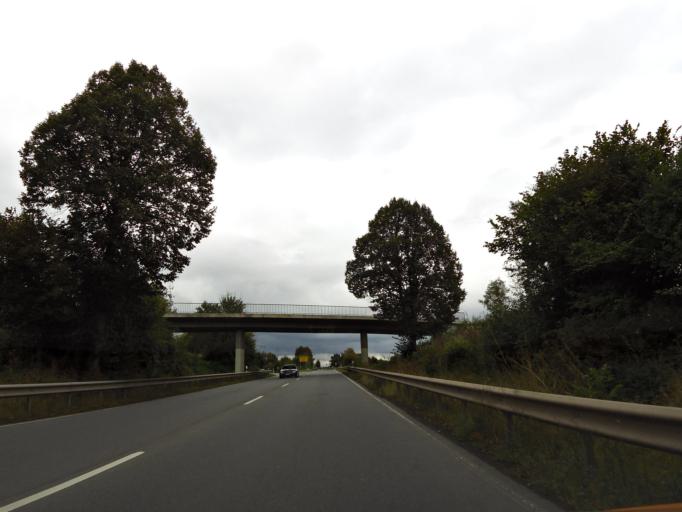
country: DE
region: Rheinland-Pfalz
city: Dreisen
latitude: 49.6055
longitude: 8.0175
